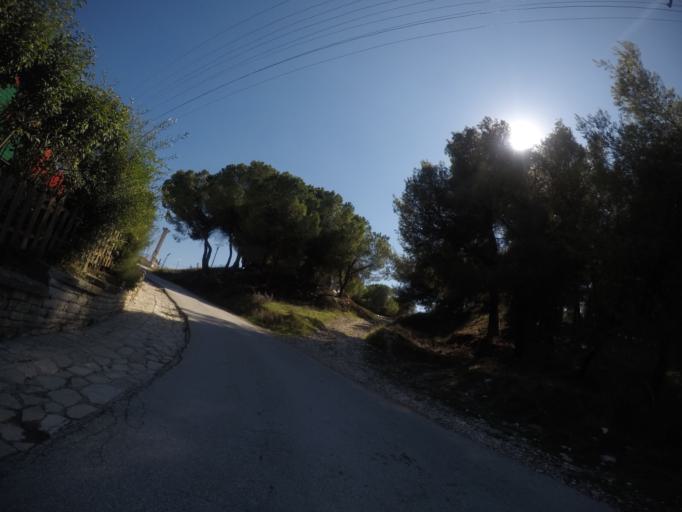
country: AL
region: Berat
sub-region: Rrethi i Beratit
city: Berat
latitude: 40.7117
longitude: 19.9461
